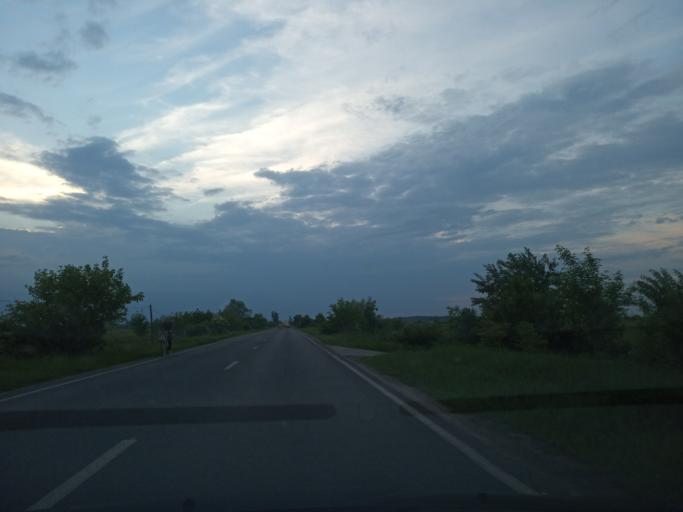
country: RO
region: Timis
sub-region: Comuna Denta
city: Denta
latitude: 45.3663
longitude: 21.2448
